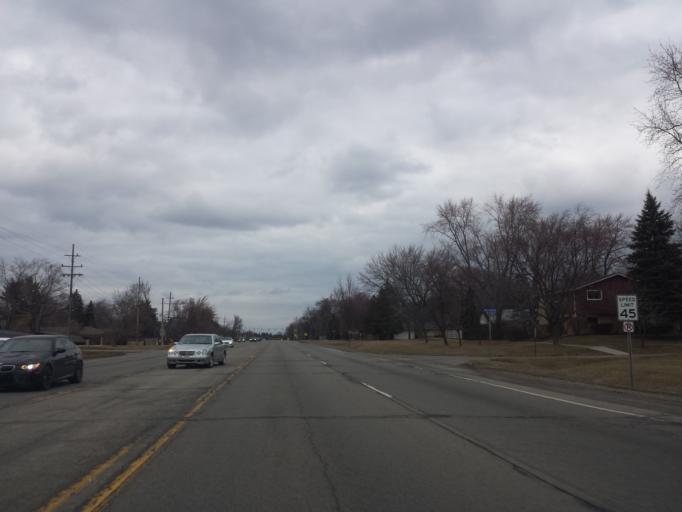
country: US
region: Michigan
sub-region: Oakland County
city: Beverly Hills
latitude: 42.5246
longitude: -83.2236
